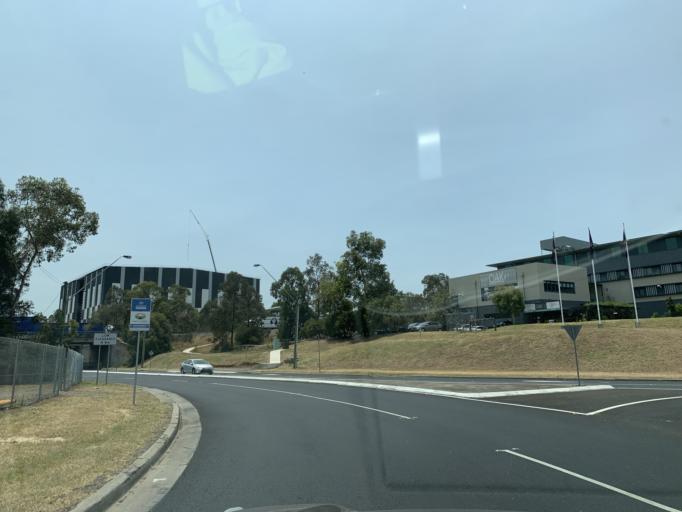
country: AU
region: New South Wales
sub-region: Blacktown
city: Doonside
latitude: -33.8022
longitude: 150.8697
